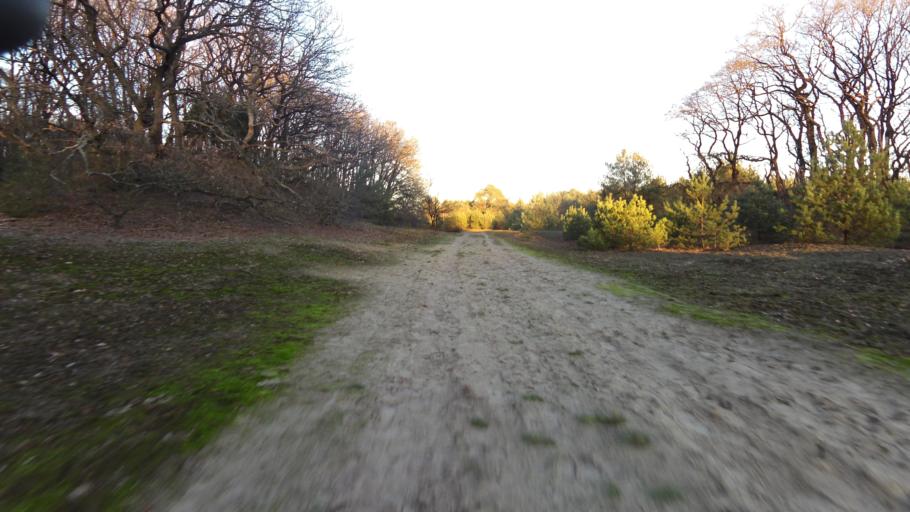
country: NL
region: Gelderland
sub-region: Gemeente Barneveld
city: Garderen
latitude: 52.2011
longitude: 5.7617
